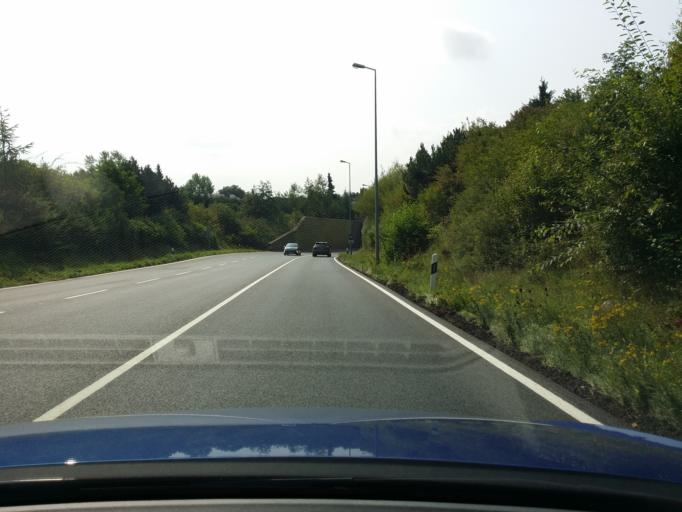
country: LU
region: Luxembourg
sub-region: Canton de Luxembourg
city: Bertrange
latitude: 49.6195
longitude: 6.0527
